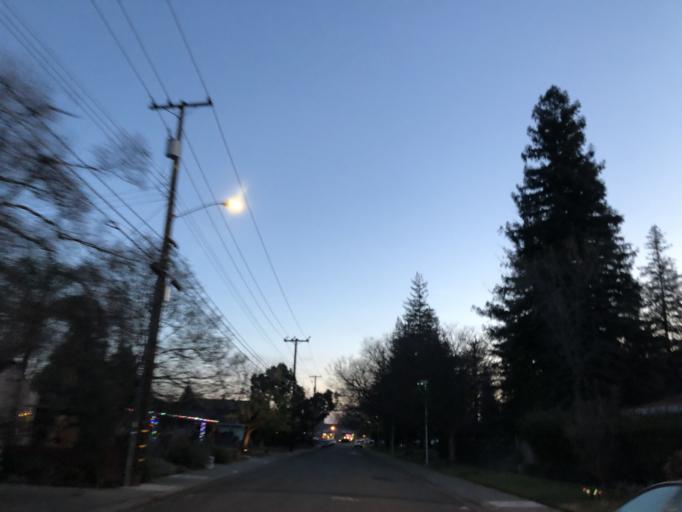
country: US
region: California
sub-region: Sacramento County
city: Parkway
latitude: 38.5486
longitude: -121.4392
